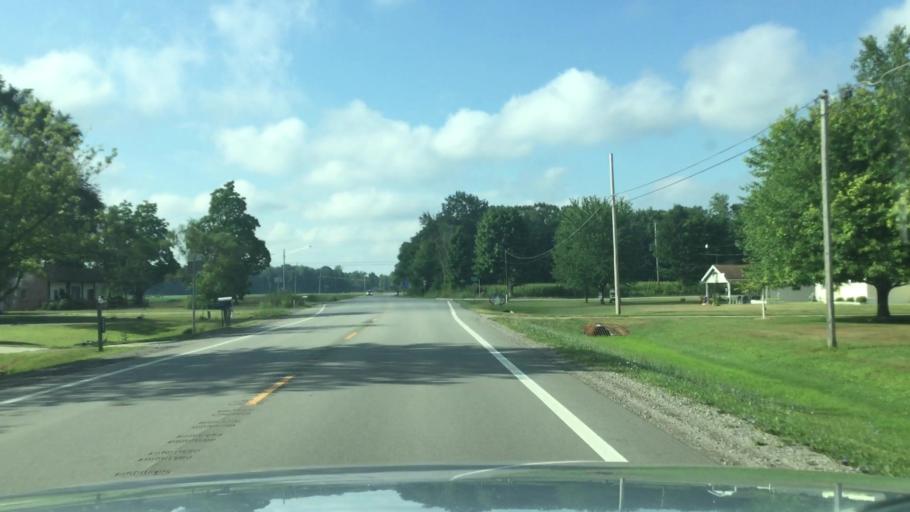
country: US
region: Michigan
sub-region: Genesee County
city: Clio
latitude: 43.2225
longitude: -83.7352
